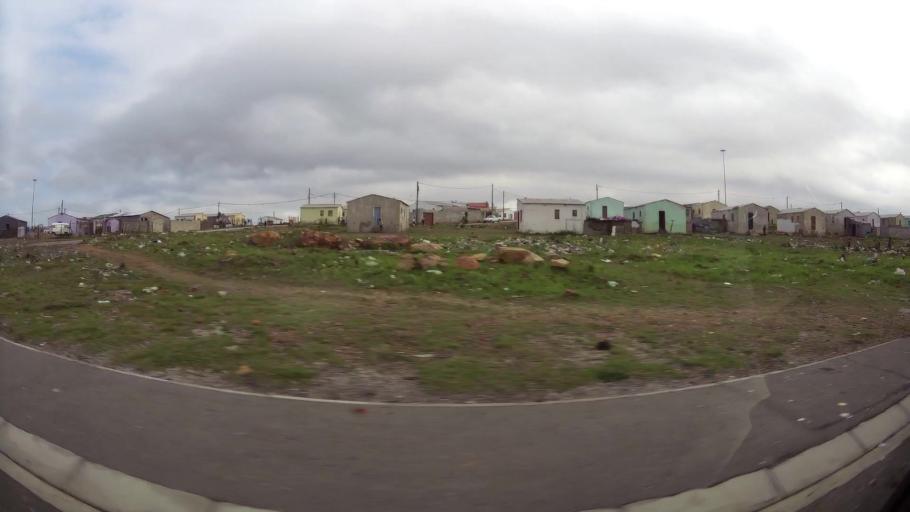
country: ZA
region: Eastern Cape
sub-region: Nelson Mandela Bay Metropolitan Municipality
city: Port Elizabeth
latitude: -33.9138
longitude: 25.5365
